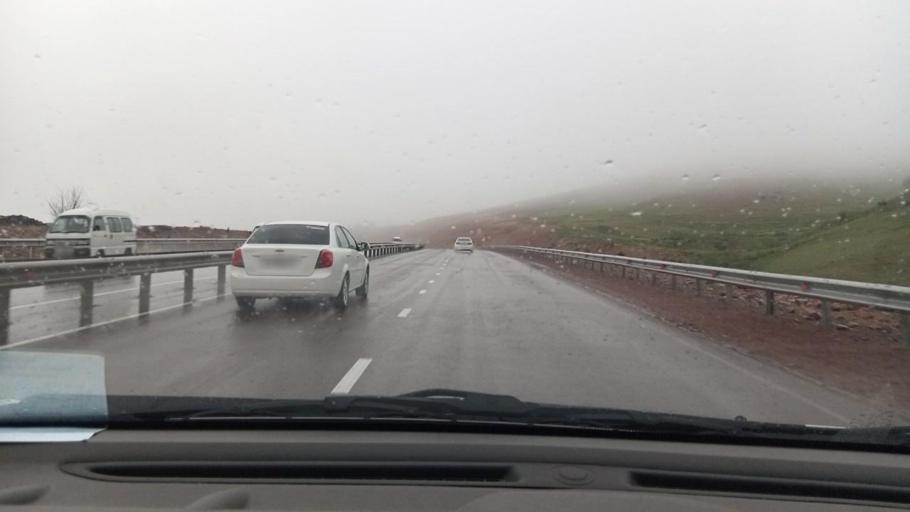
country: UZ
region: Toshkent
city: Angren
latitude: 41.0608
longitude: 70.1842
